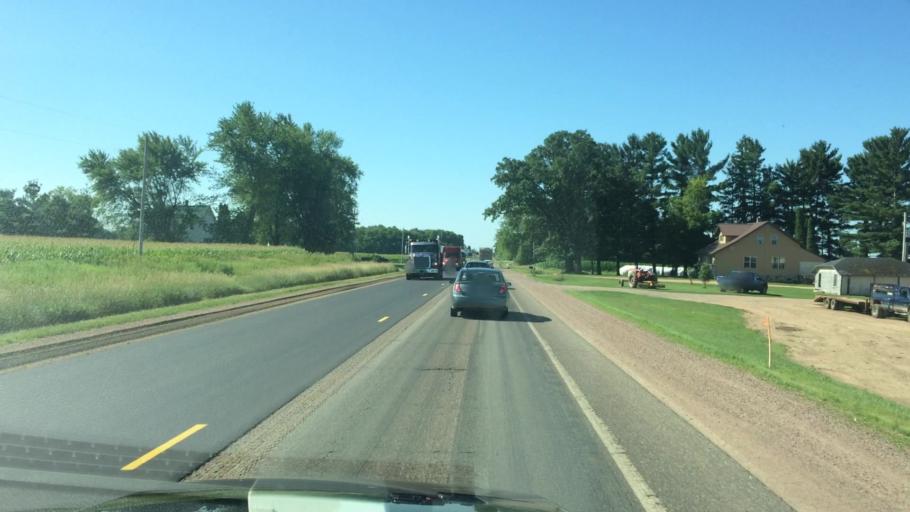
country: US
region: Wisconsin
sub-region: Marathon County
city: Stratford
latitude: 44.8640
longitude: -90.0791
